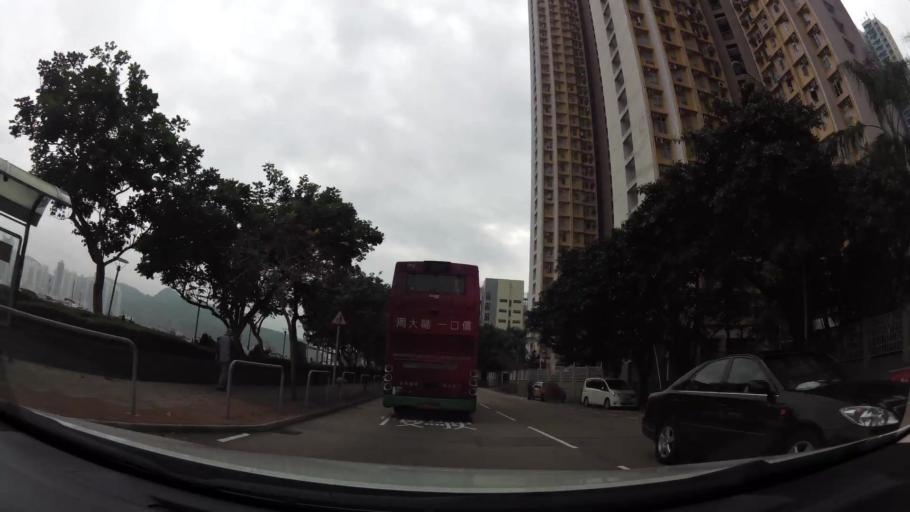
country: HK
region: Wanchai
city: Wan Chai
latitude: 22.2828
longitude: 114.2271
